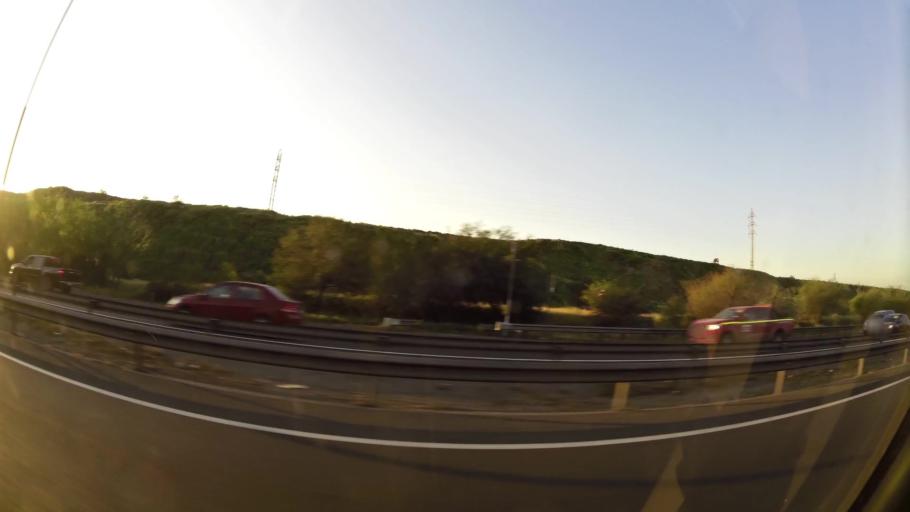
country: CL
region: Santiago Metropolitan
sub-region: Provincia de Santiago
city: Lo Prado
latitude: -33.4826
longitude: -70.7113
